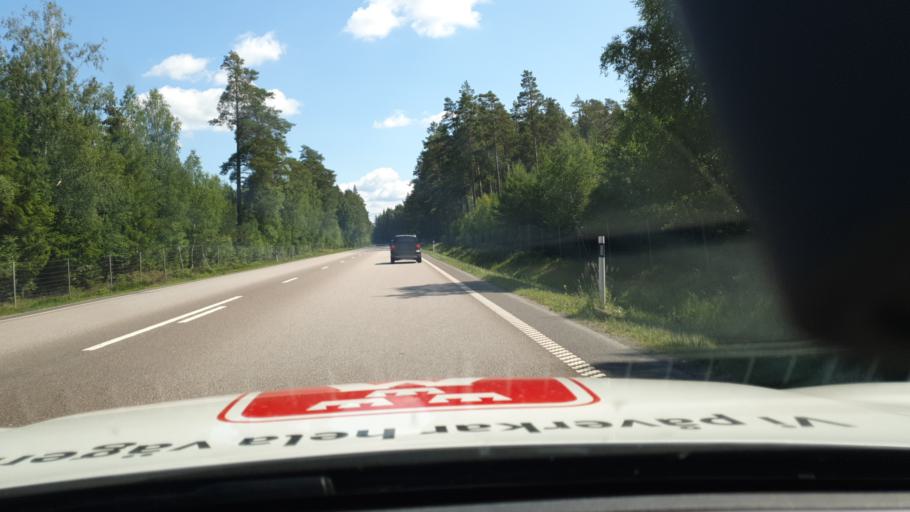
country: SE
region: Vaestra Goetaland
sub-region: Lidkopings Kommun
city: Lidkoping
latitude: 58.4730
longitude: 13.2089
